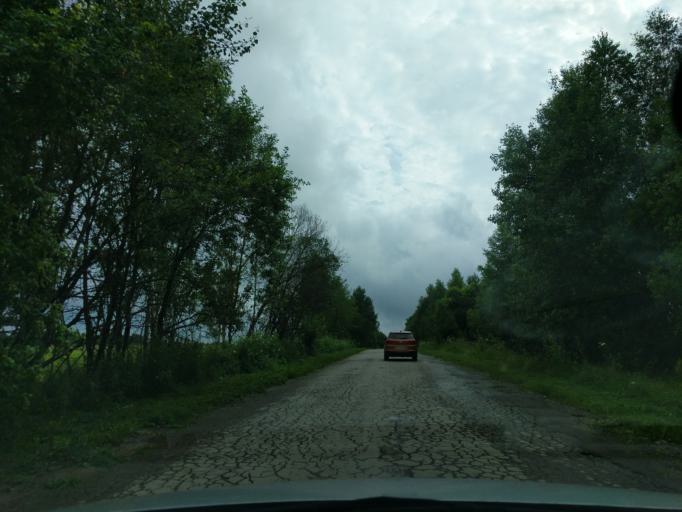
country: RU
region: Kaluga
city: Nikola-Lenivets
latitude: 54.7558
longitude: 35.6984
